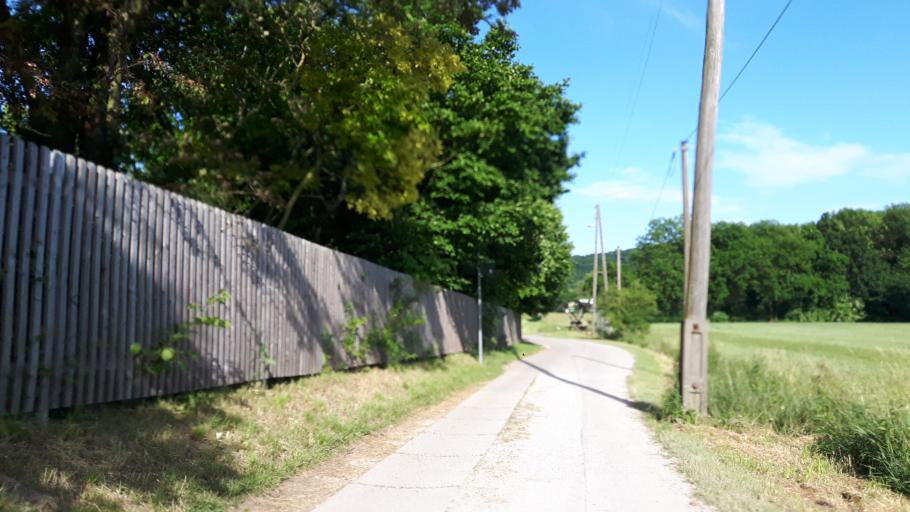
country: DE
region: Saxony-Anhalt
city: Bad Kosen
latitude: 51.1499
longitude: 11.7458
